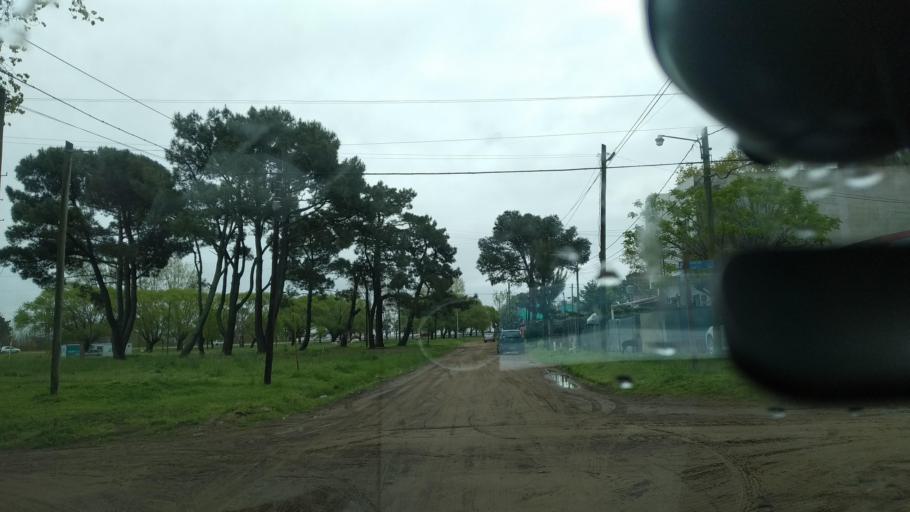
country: AR
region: Buenos Aires
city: Mar del Tuyu
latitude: -36.5313
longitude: -56.7142
